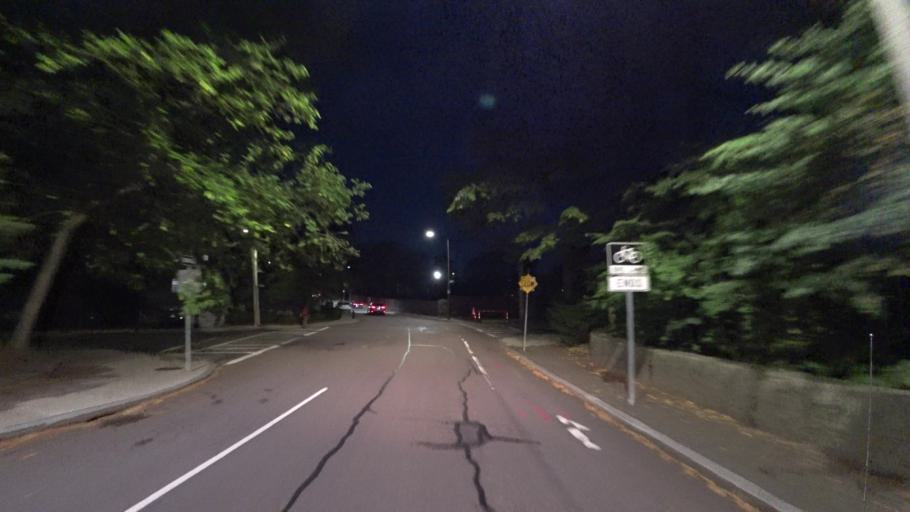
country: US
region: Massachusetts
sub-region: Middlesex County
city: Watertown
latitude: 42.3452
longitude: -71.1631
